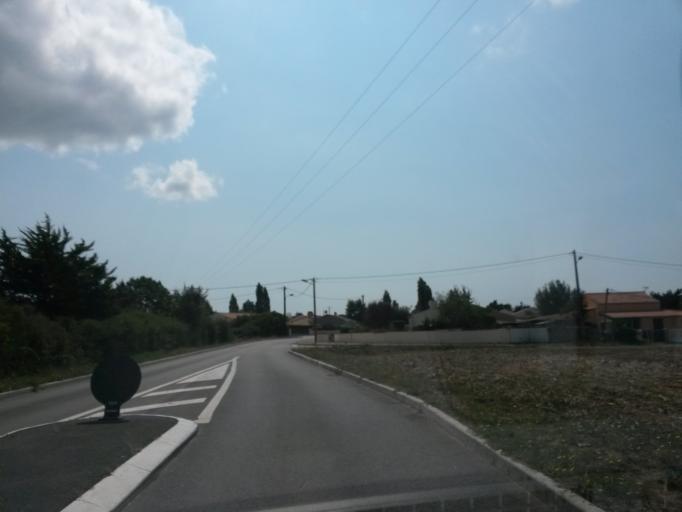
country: FR
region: Pays de la Loire
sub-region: Departement de la Vendee
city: Saint-Hilaire-de-Talmont
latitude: 46.4497
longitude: -1.6246
